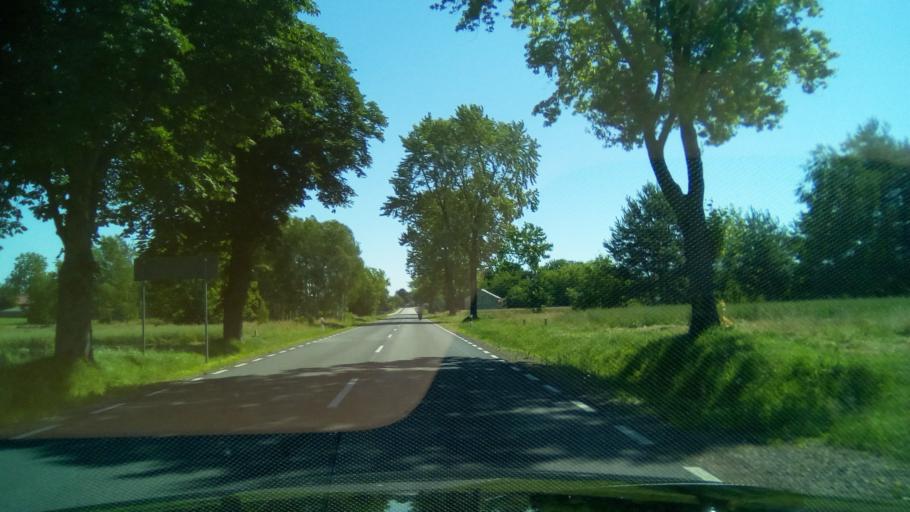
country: PL
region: Masovian Voivodeship
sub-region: Powiat przysuski
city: Odrzywol
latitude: 51.5200
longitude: 20.5086
